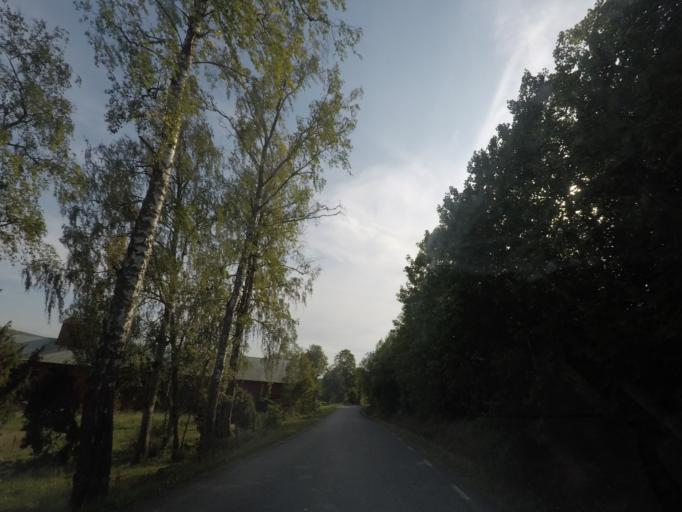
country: SE
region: Vaestmanland
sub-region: Kungsors Kommun
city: Kungsoer
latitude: 59.5059
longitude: 16.1562
